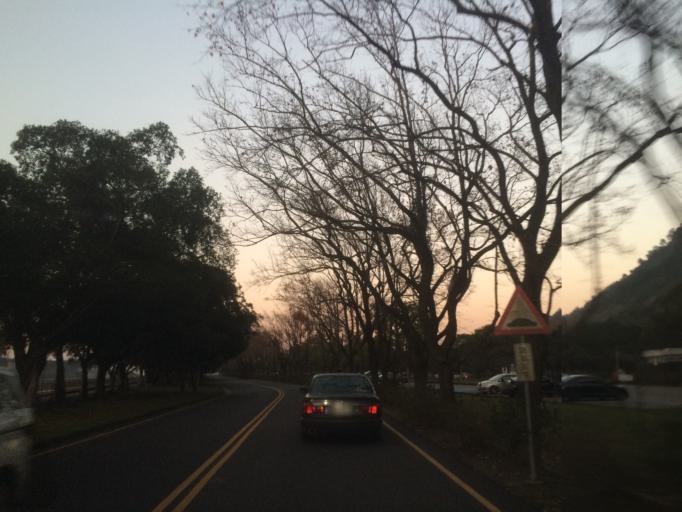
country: TW
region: Taiwan
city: Daxi
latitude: 24.8139
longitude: 121.2466
